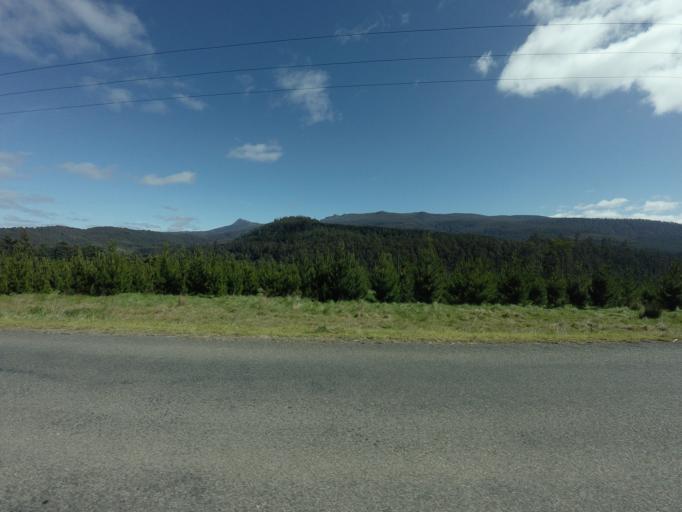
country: AU
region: Tasmania
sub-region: Derwent Valley
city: New Norfolk
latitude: -42.7465
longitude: 146.6512
